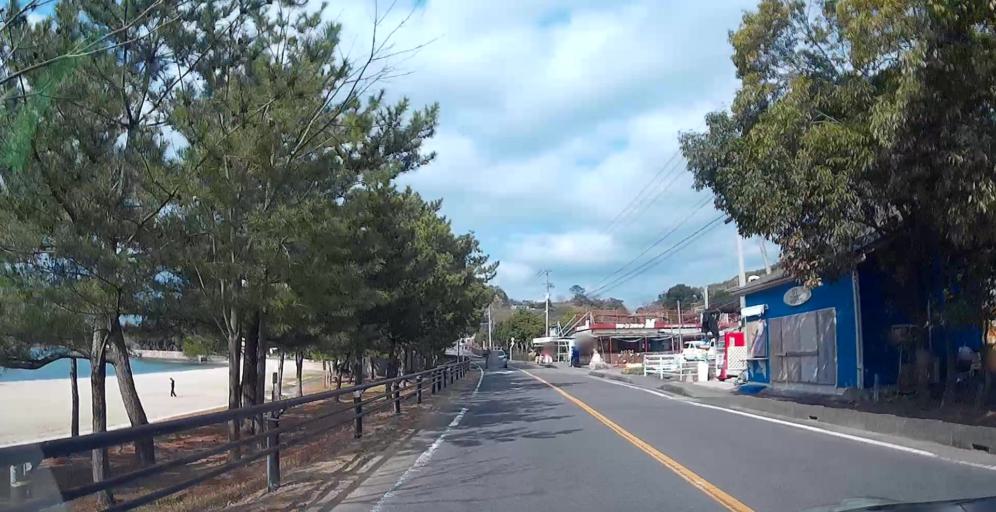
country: JP
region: Kumamoto
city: Minamata
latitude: 32.3175
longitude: 130.4717
